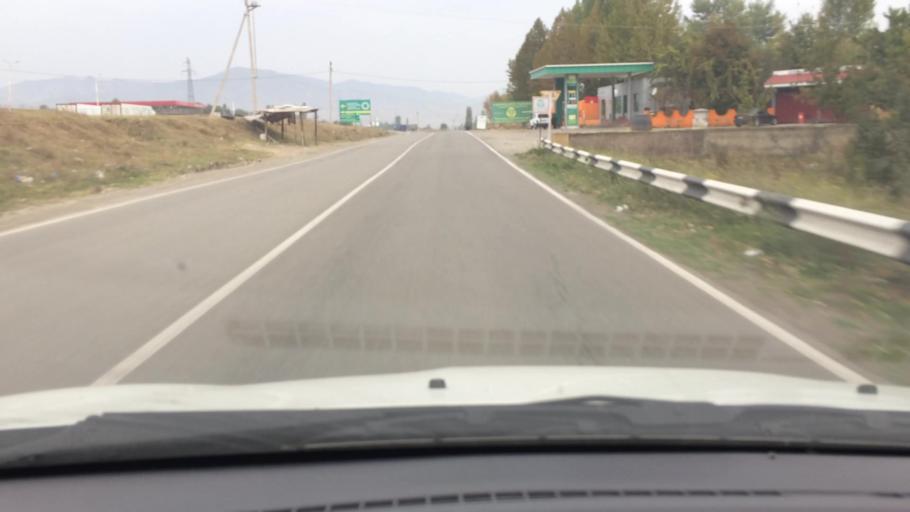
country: AM
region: Tavush
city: Bagratashen
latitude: 41.2311
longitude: 44.8189
